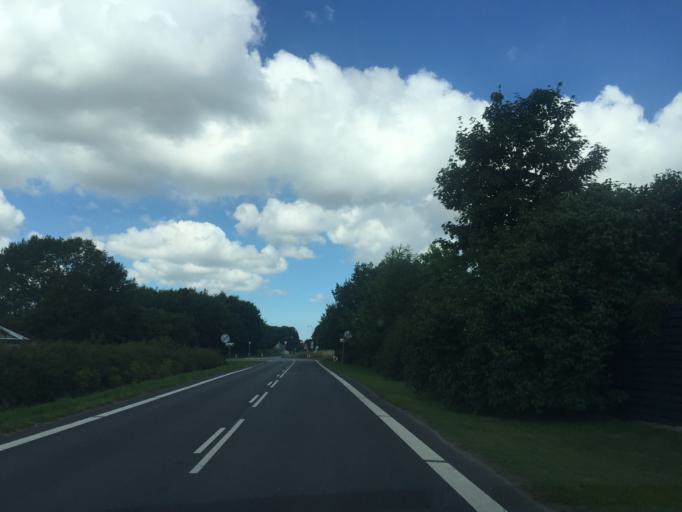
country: DK
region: South Denmark
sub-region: Nordfyns Kommune
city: Otterup
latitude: 55.5248
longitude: 10.3954
